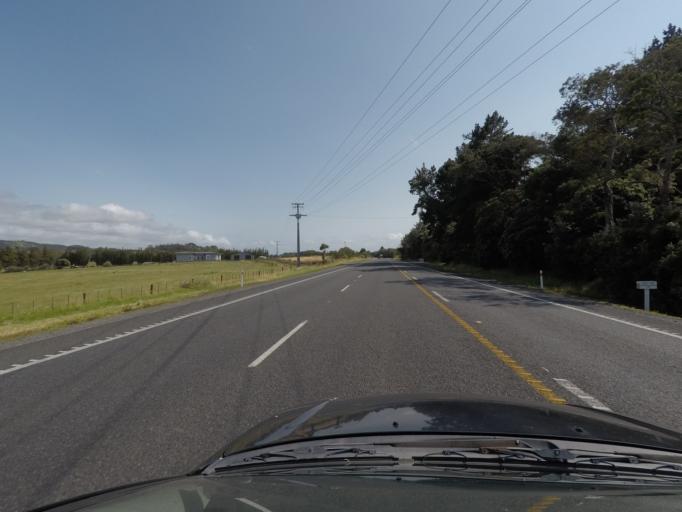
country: NZ
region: Northland
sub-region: Whangarei
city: Ruakaka
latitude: -35.9493
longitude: 174.4540
